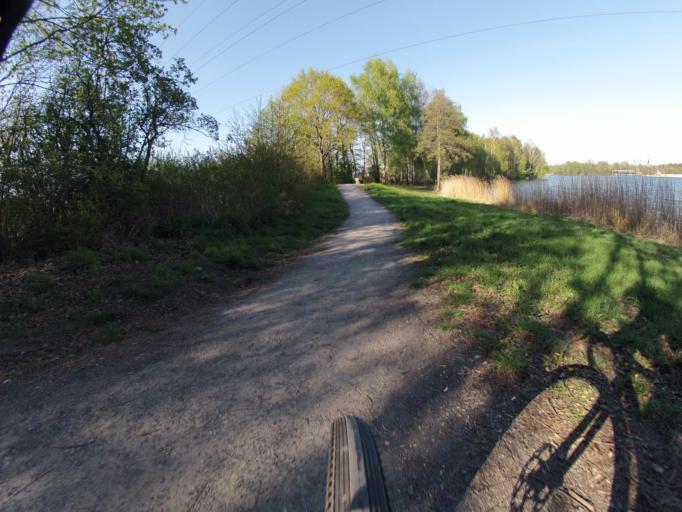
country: DE
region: Lower Saxony
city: Schuttorf
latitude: 52.3369
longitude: 7.2148
